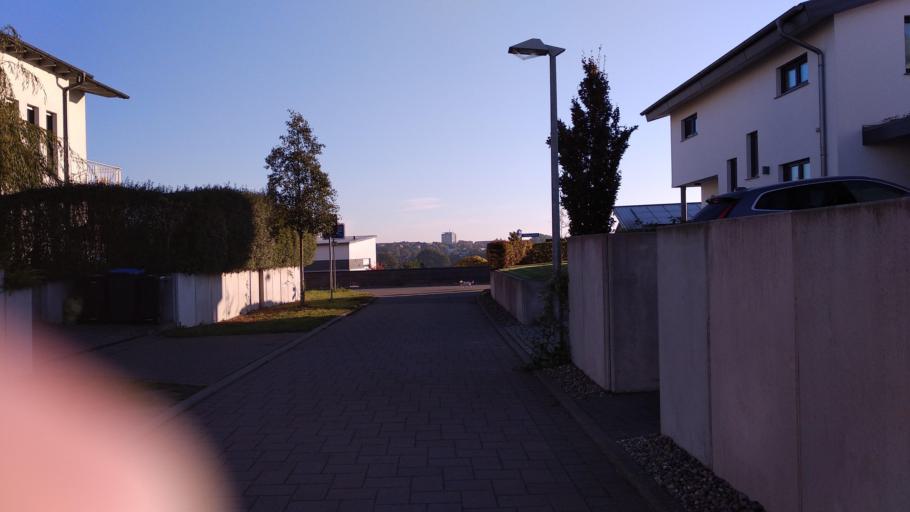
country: DE
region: Mecklenburg-Vorpommern
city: Neumuehle
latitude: 53.6228
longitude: 11.3761
